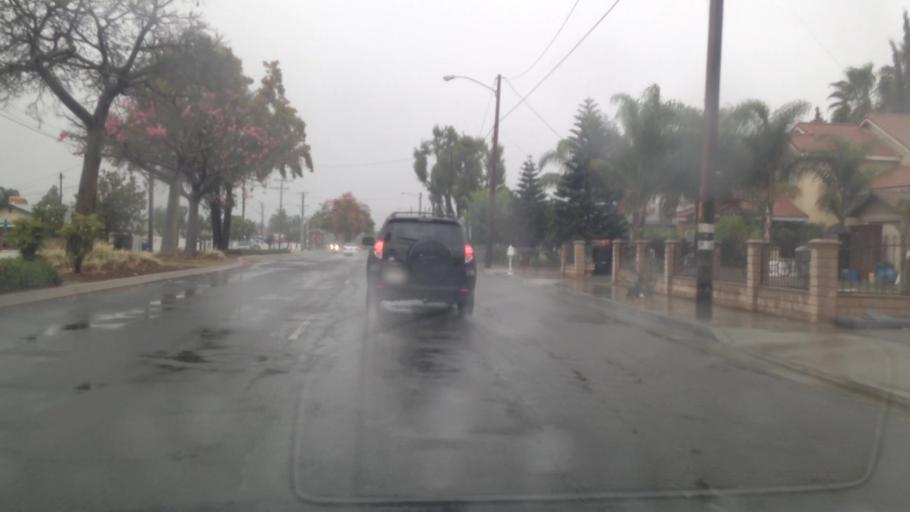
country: US
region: California
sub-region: Riverside County
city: Home Gardens
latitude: 33.9228
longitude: -117.4911
